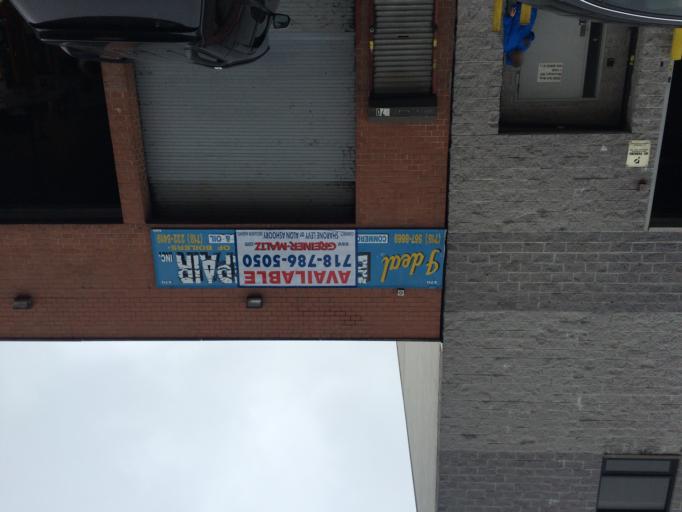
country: US
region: New York
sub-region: Kings County
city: Bensonhurst
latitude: 40.6470
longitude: -74.0163
